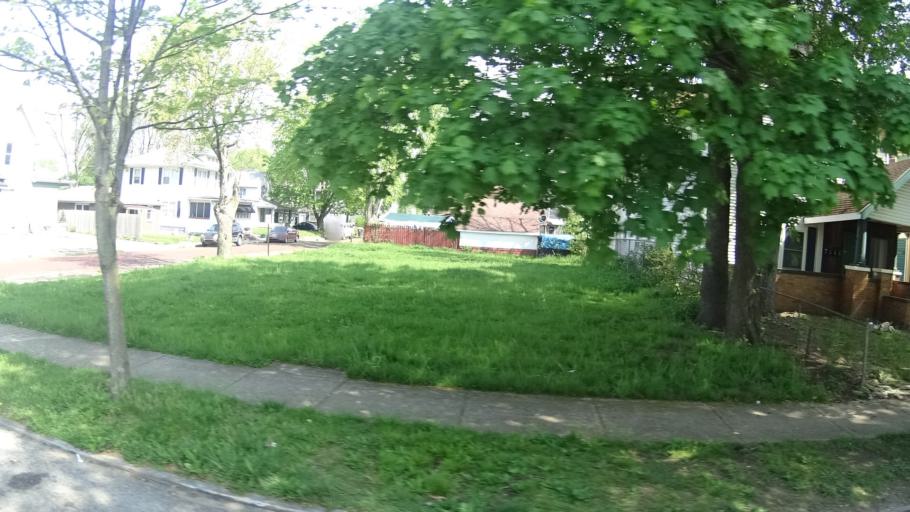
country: US
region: Indiana
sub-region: Madison County
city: Anderson
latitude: 40.1051
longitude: -85.6856
